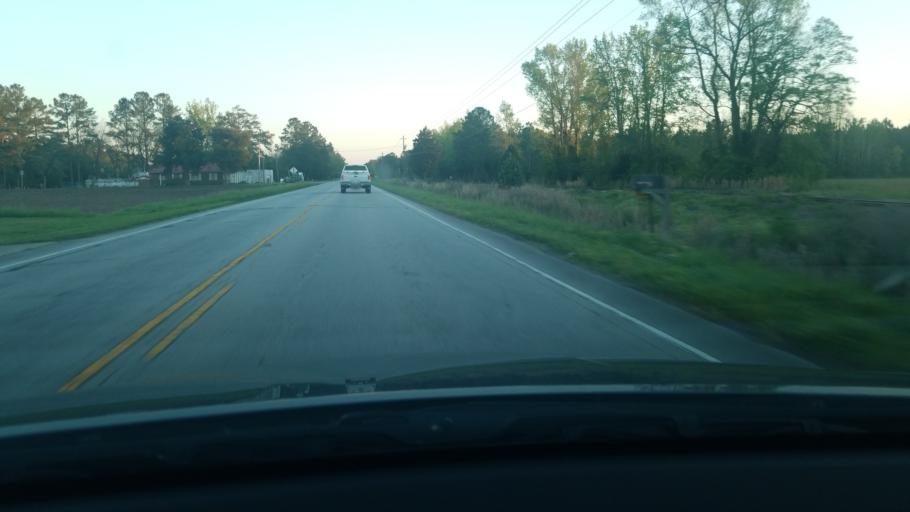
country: US
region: North Carolina
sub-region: Craven County
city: Vanceboro
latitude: 35.3469
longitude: -77.1510
